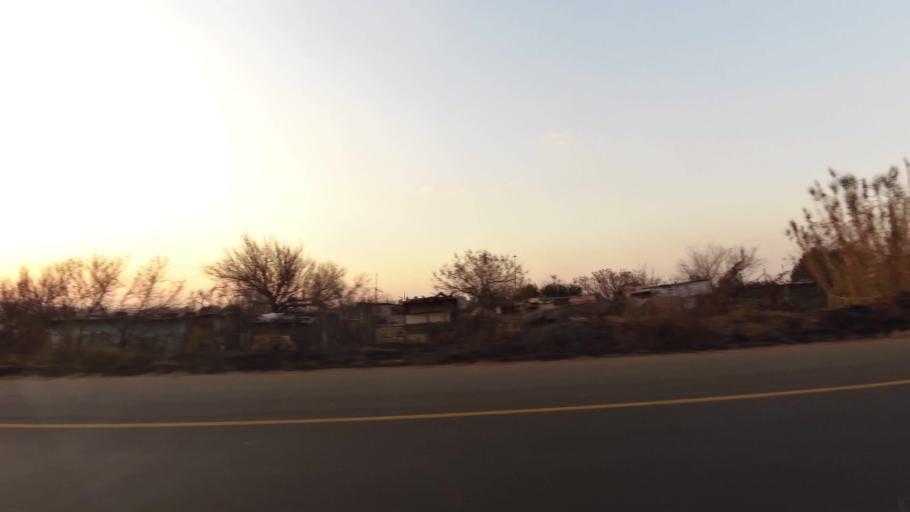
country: ZA
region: Gauteng
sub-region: City of Johannesburg Metropolitan Municipality
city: Soweto
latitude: -26.2895
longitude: 27.8875
